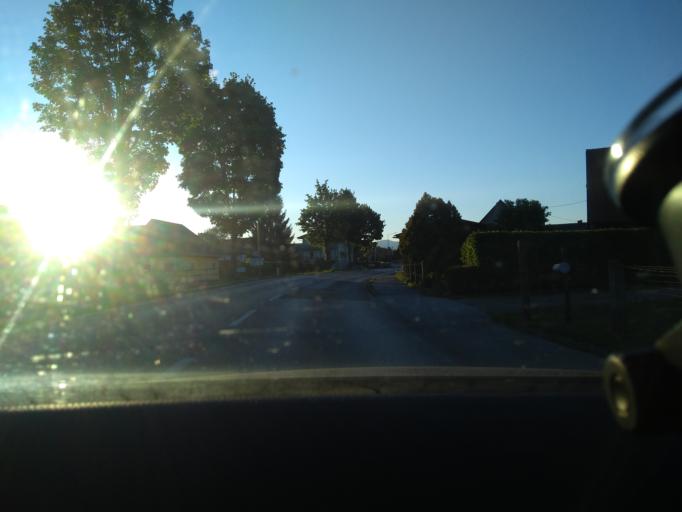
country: AT
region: Styria
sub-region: Politischer Bezirk Voitsberg
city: Mooskirchen
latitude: 46.9986
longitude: 15.2927
